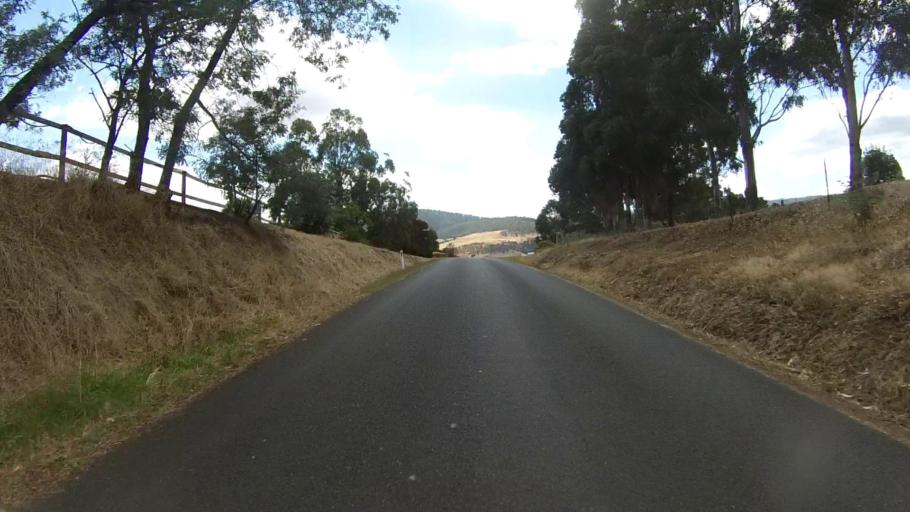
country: AU
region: Tasmania
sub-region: Derwent Valley
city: New Norfolk
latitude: -42.7519
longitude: 146.9720
